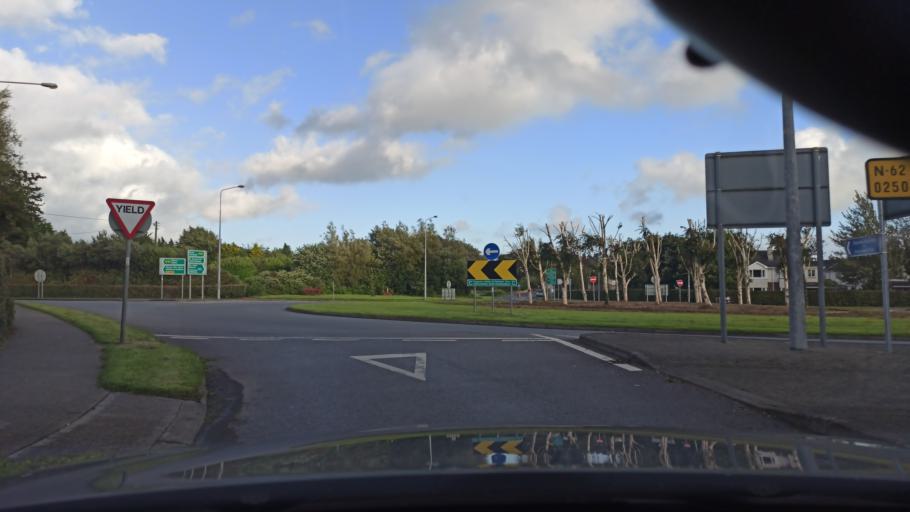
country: IE
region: Munster
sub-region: North Tipperary
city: Roscrea
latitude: 52.9474
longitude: -7.7965
